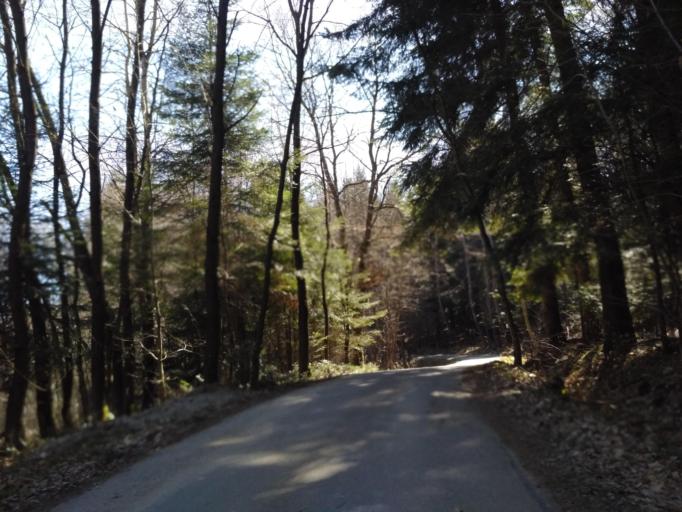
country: PL
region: Subcarpathian Voivodeship
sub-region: Powiat brzozowski
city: Zmiennica
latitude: 49.7071
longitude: 21.9669
